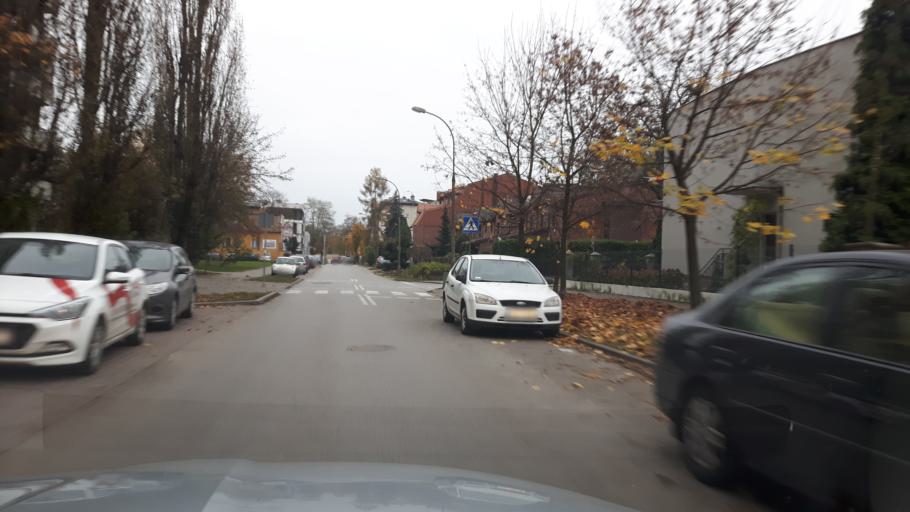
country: PL
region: Masovian Voivodeship
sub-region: Warszawa
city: Targowek
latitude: 52.2861
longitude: 21.0294
